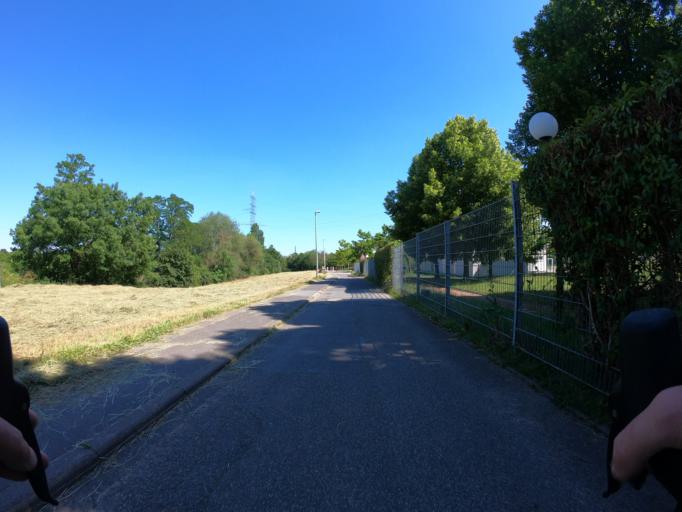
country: DE
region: Hesse
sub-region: Regierungsbezirk Darmstadt
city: Eschborn
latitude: 50.1351
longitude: 8.5776
